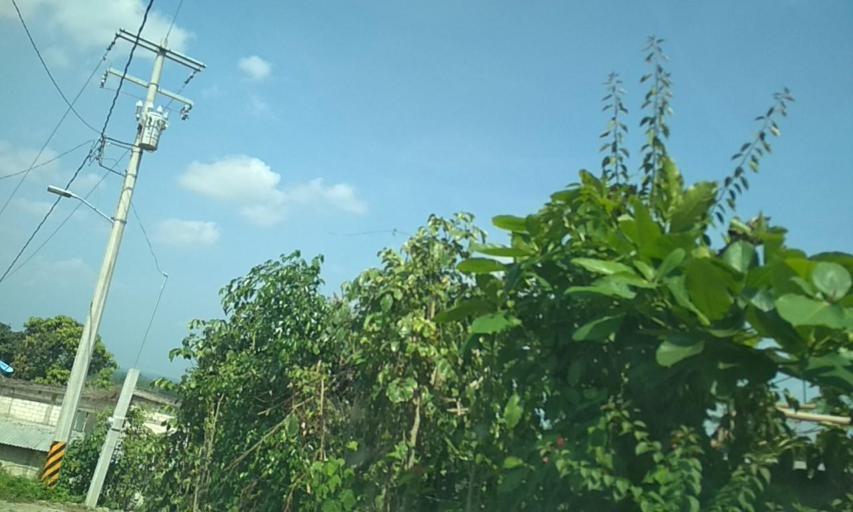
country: MX
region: Veracruz
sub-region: Atzalan
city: Colonias Pedernales
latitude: 20.0546
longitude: -97.0192
